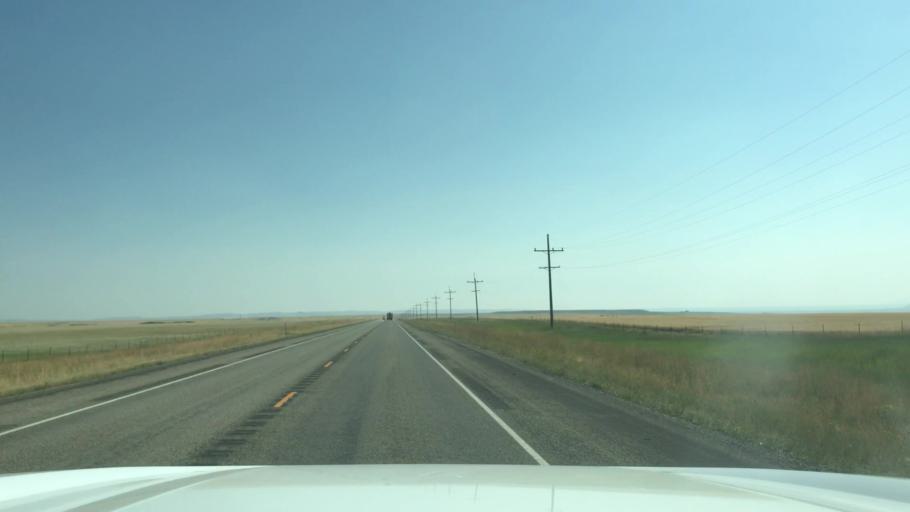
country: US
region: Montana
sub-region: Wheatland County
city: Harlowton
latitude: 46.5086
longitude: -109.7661
